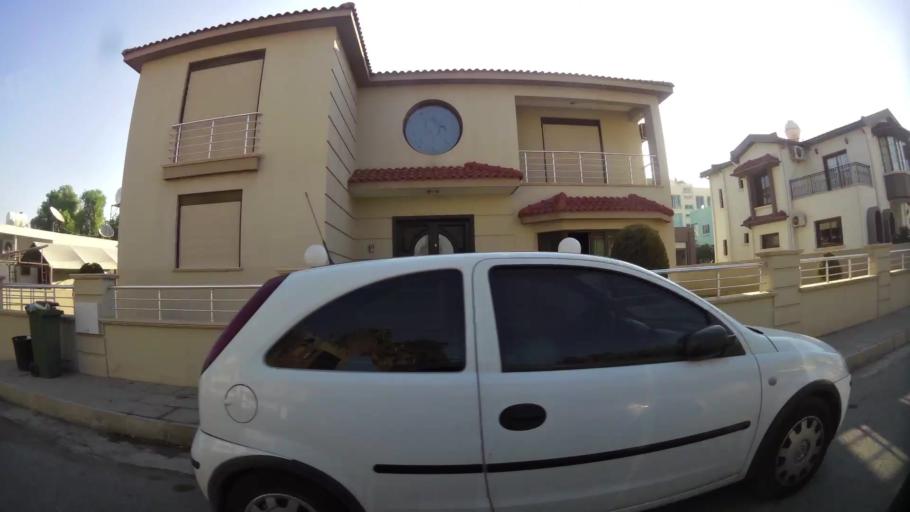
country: CY
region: Lefkosia
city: Nicosia
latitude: 35.2035
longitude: 33.3485
